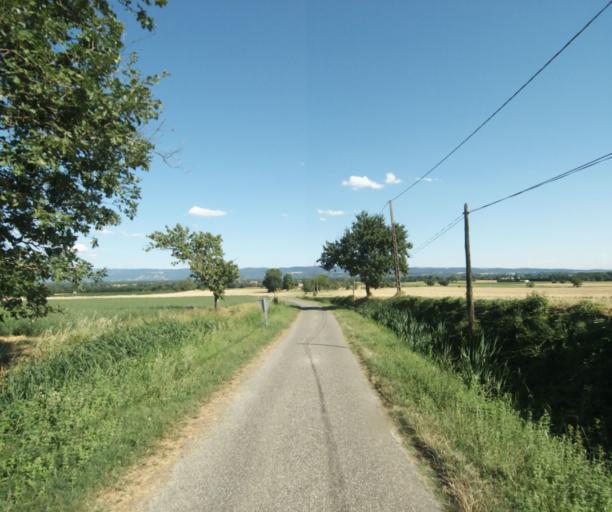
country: FR
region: Midi-Pyrenees
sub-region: Departement de la Haute-Garonne
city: Saint-Felix-Lauragais
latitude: 43.4935
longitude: 1.9421
